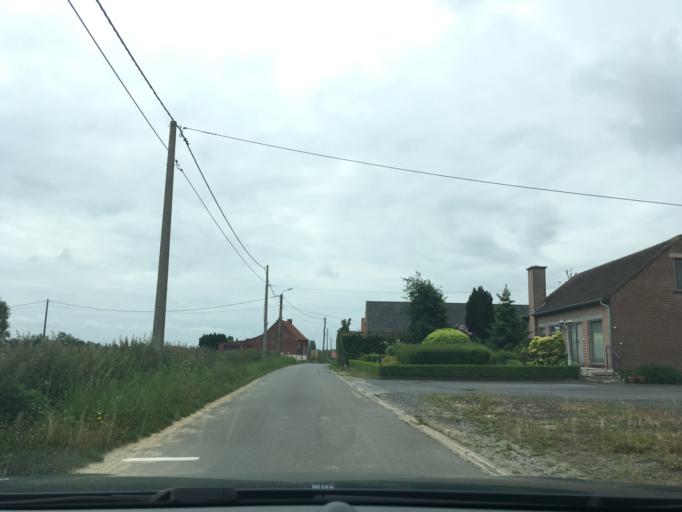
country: BE
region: Flanders
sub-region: Provincie West-Vlaanderen
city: Ledegem
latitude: 50.8868
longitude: 3.1061
